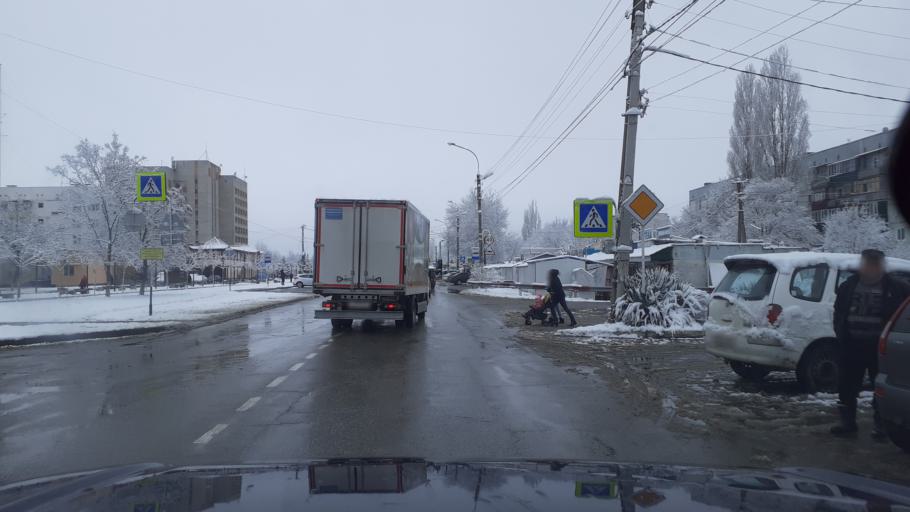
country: RU
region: Adygeya
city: Maykop
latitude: 44.5771
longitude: 40.1320
